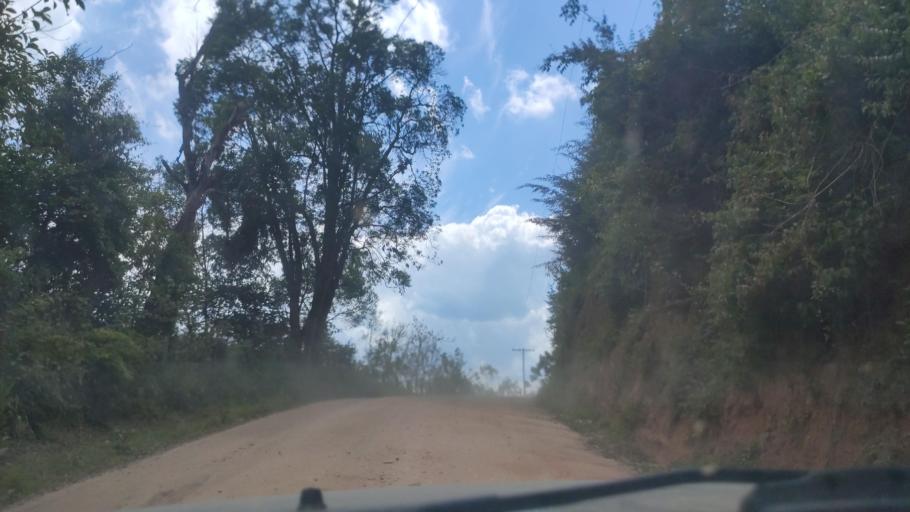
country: BR
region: Minas Gerais
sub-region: Cambui
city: Cambui
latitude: -22.7053
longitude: -46.0193
